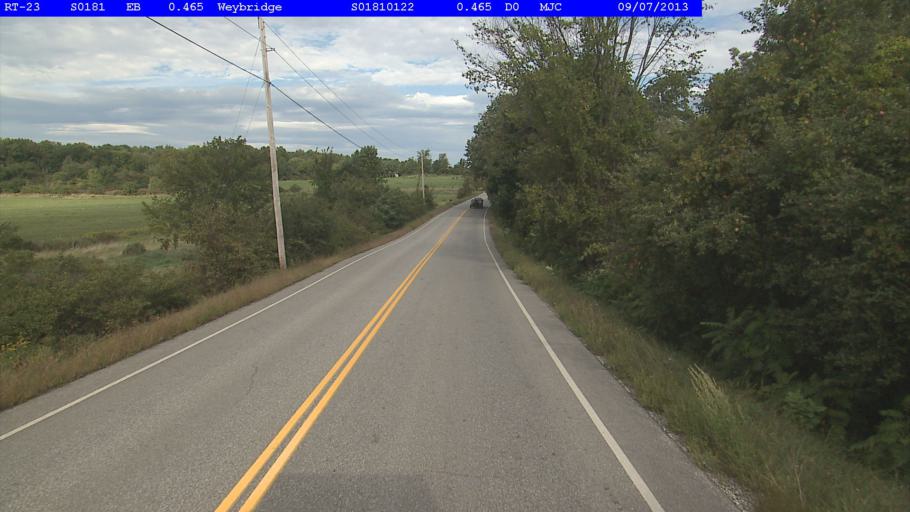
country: US
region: Vermont
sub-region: Addison County
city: Middlebury (village)
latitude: 44.0229
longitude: -73.1901
